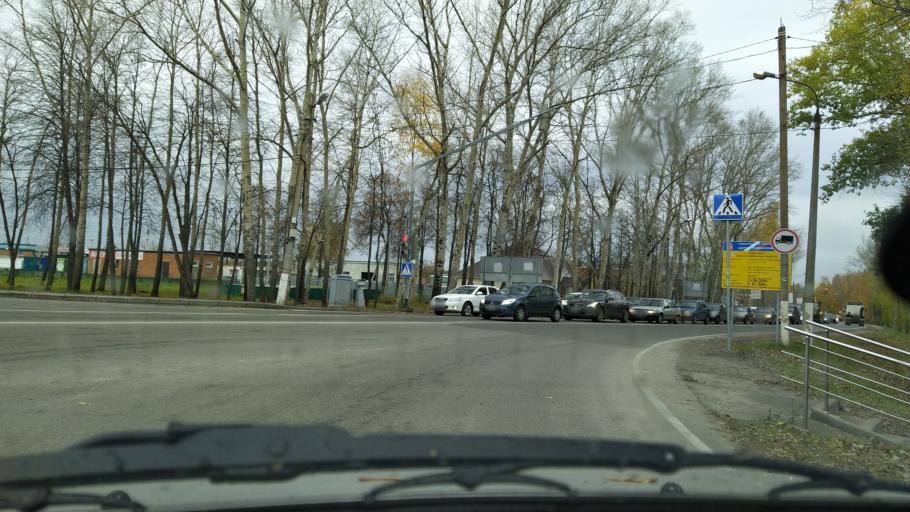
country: RU
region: Moskovskaya
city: Voskresensk
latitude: 55.3171
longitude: 38.6483
